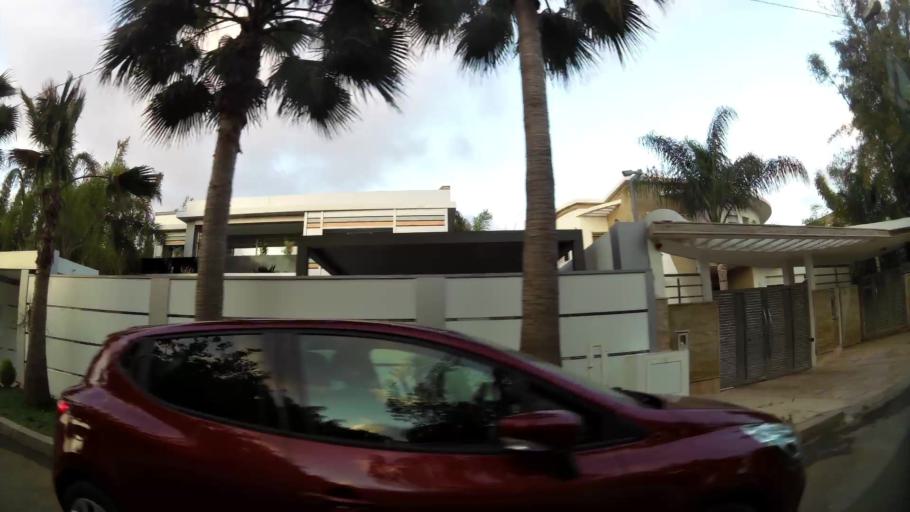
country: MA
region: Rabat-Sale-Zemmour-Zaer
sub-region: Rabat
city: Rabat
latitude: 33.9690
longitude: -6.8318
